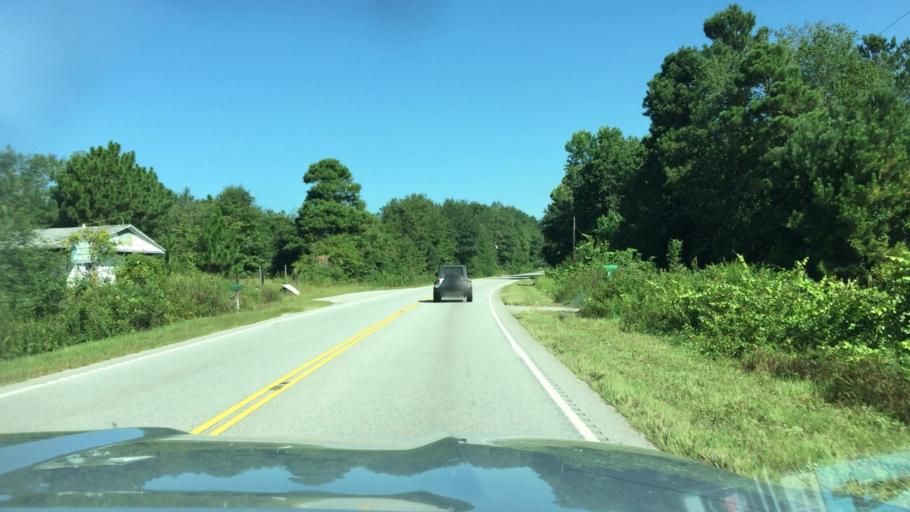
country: US
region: South Carolina
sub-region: Chesterfield County
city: Cheraw
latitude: 34.6254
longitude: -79.8820
